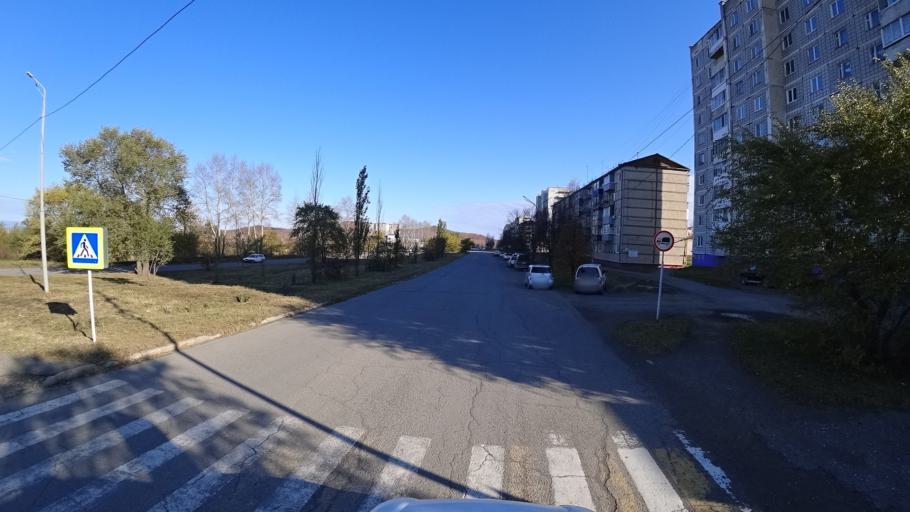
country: RU
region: Khabarovsk Krai
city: Amursk
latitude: 50.2439
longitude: 136.9152
